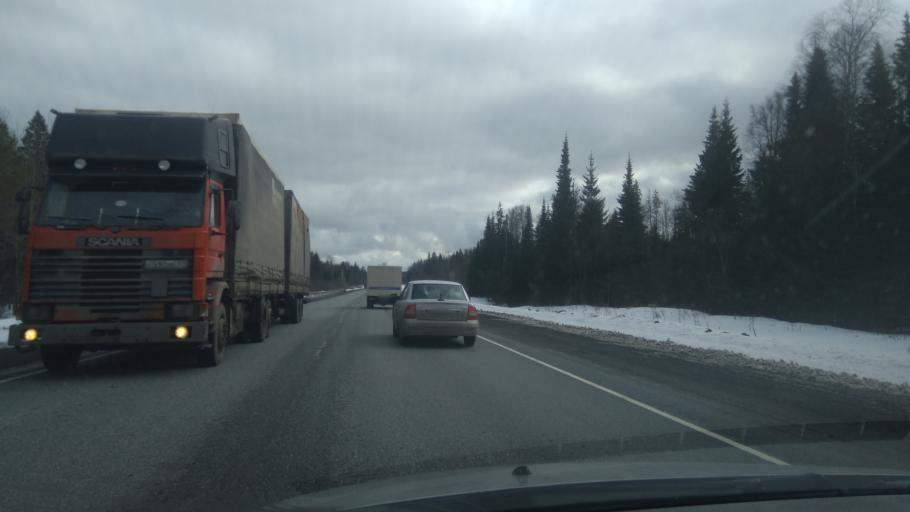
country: RU
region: Sverdlovsk
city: Atig
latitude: 56.8137
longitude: 59.3582
